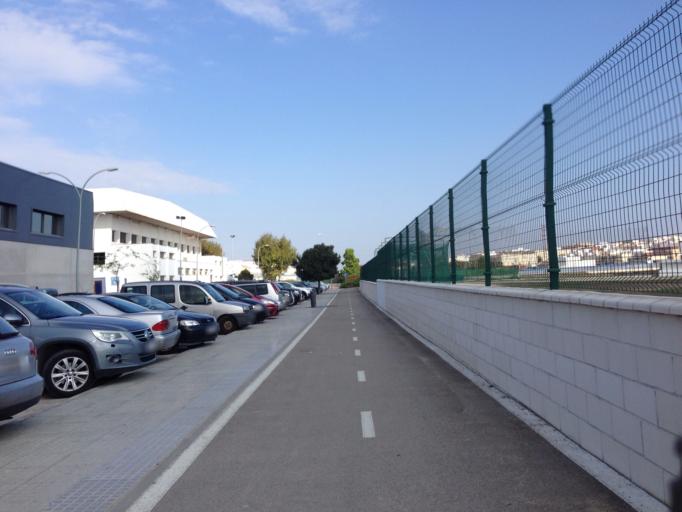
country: ES
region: Andalusia
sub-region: Provincia de Cadiz
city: Chiclana de la Frontera
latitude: 36.4129
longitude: -6.1399
